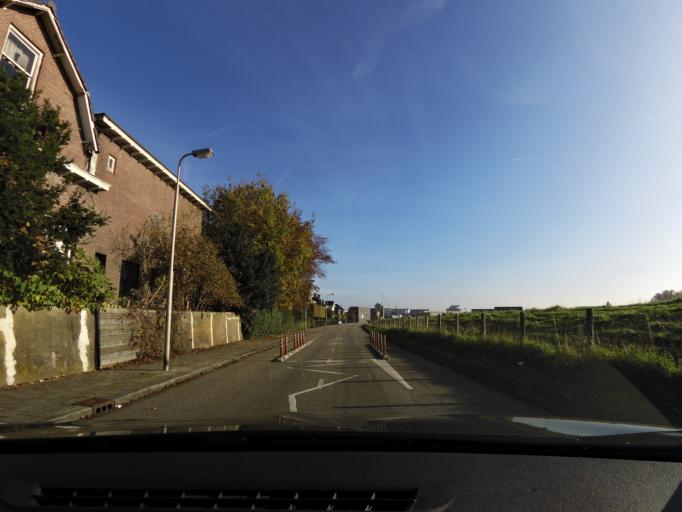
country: NL
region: South Holland
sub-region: Gemeente Ridderkerk
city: Ridderkerk
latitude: 51.8887
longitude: 4.6125
